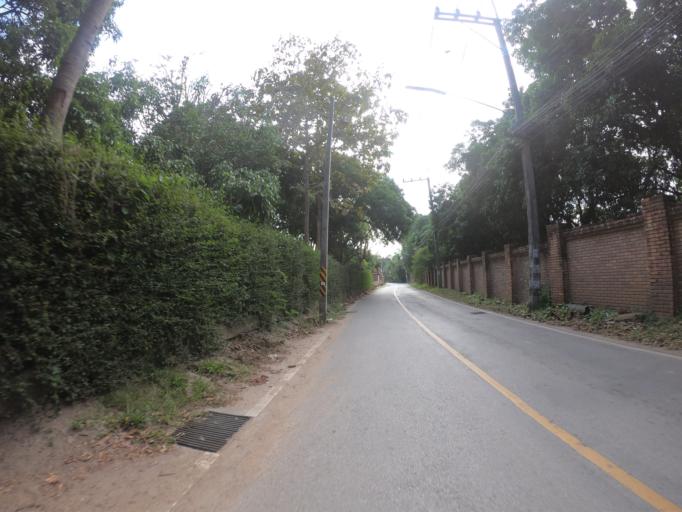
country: TH
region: Chiang Mai
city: Chiang Mai
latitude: 18.8183
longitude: 98.9532
